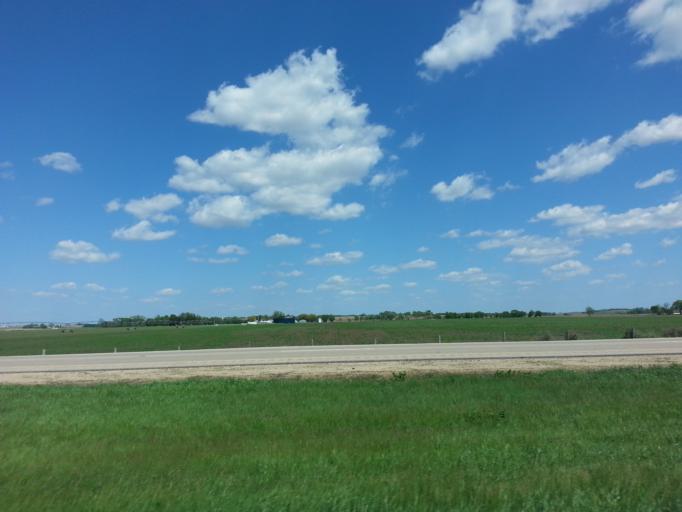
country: US
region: Wisconsin
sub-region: Rock County
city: Janesville
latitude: 42.6305
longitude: -88.9828
